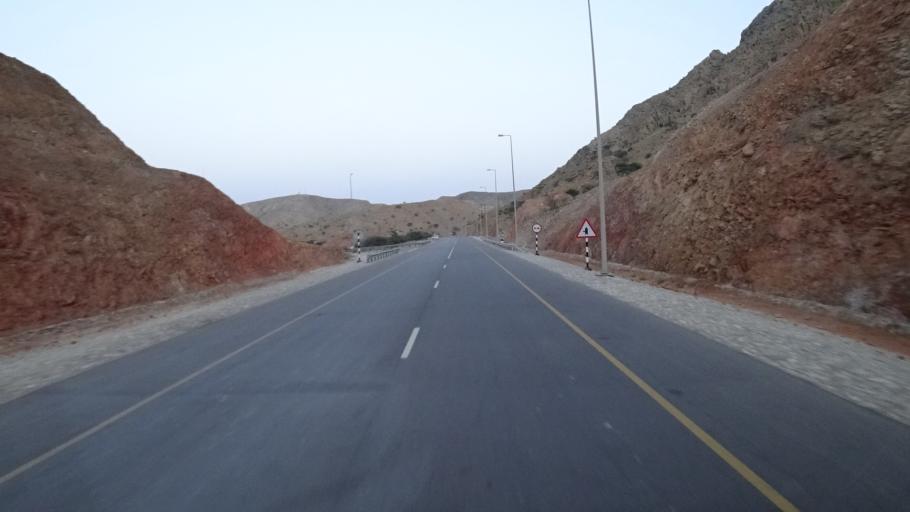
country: OM
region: Muhafazat Masqat
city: Muscat
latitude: 23.5077
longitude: 58.7264
